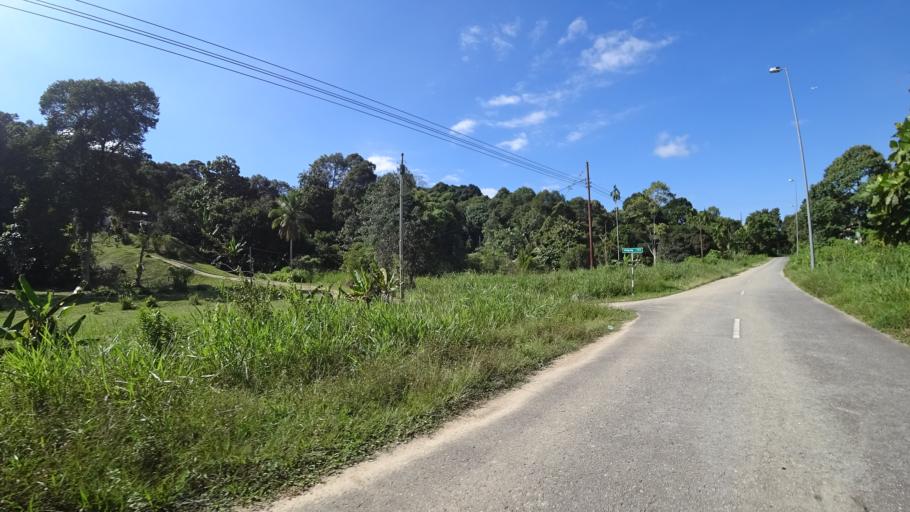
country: BN
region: Tutong
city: Tutong
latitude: 4.7362
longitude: 114.7907
